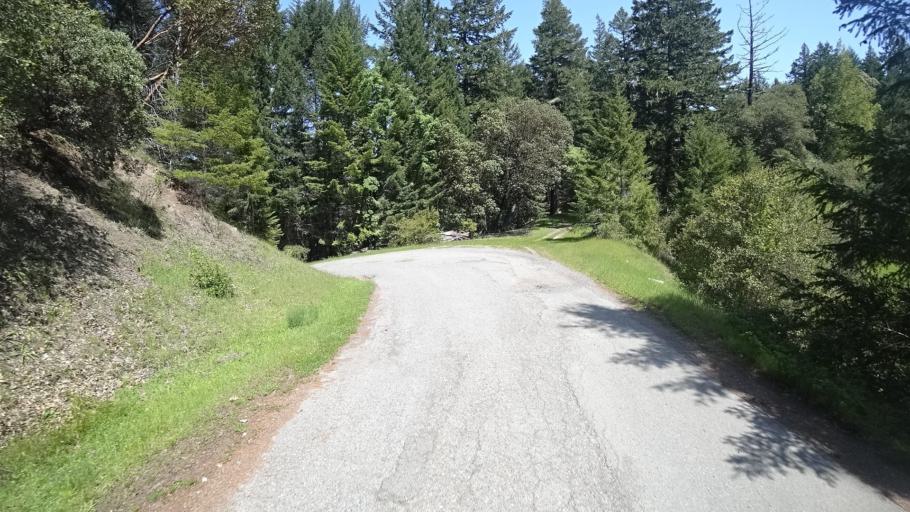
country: US
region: California
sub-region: Humboldt County
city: Redway
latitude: 40.2123
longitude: -123.6575
